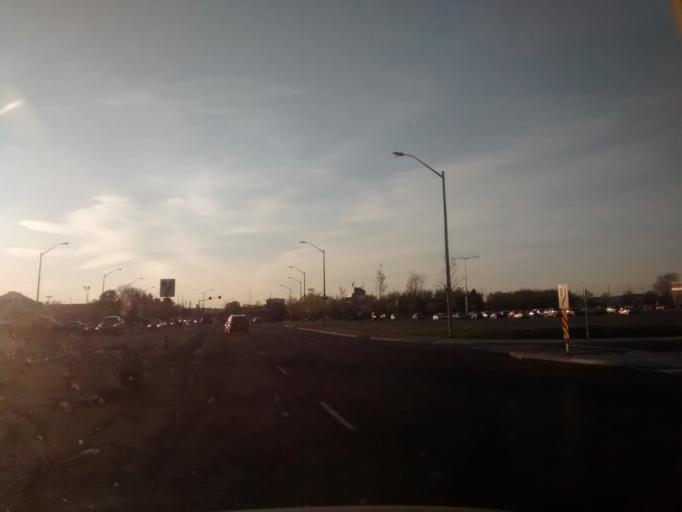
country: CA
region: Ontario
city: Burlington
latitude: 43.3457
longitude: -79.7953
